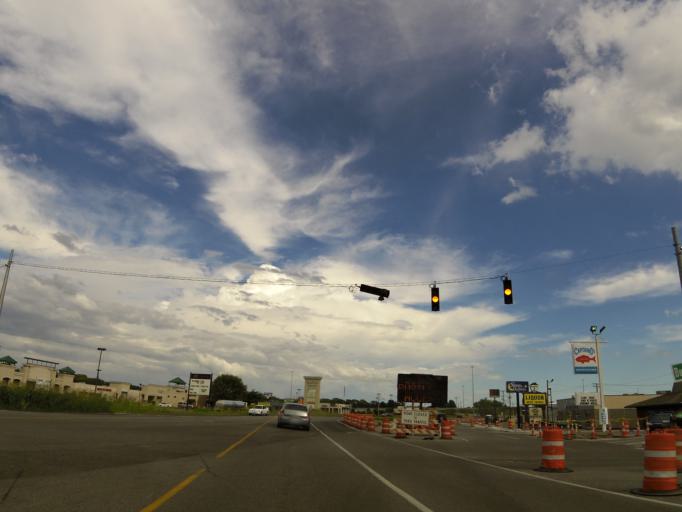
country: US
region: Kentucky
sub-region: Christian County
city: Hopkinsville
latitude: 36.8360
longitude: -87.4761
